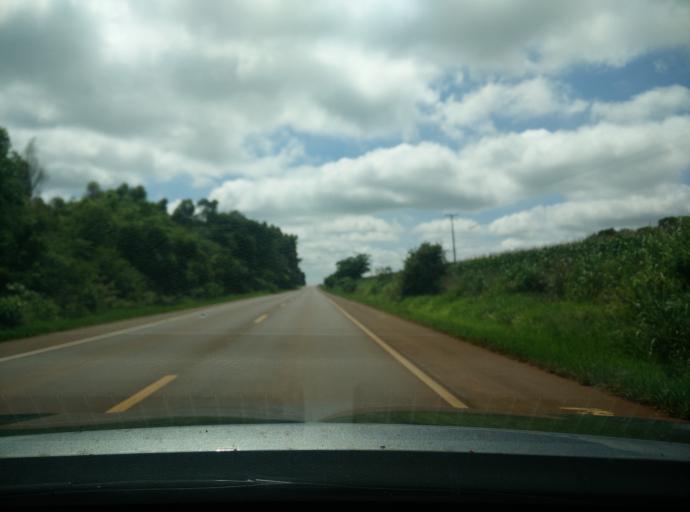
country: BR
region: Parana
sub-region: Campo Mourao
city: Campo Mourao
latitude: -23.9845
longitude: -52.5260
